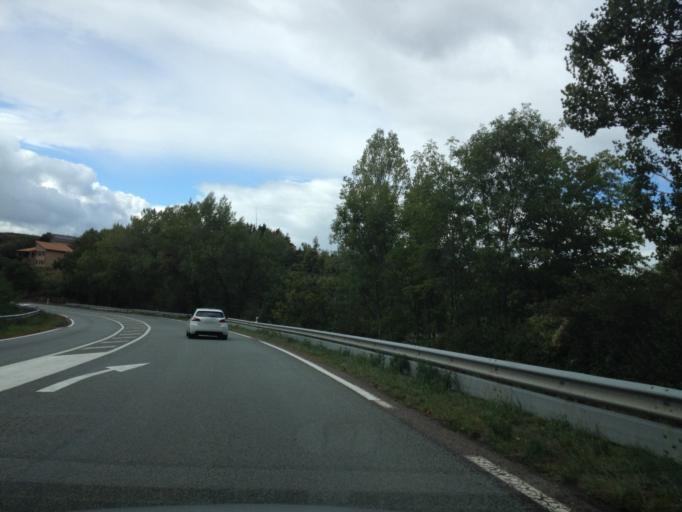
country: FR
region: Rhone-Alpes
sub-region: Departement de la Loire
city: Saint-Symphorien-de-Lay
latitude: 45.9656
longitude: 4.1678
